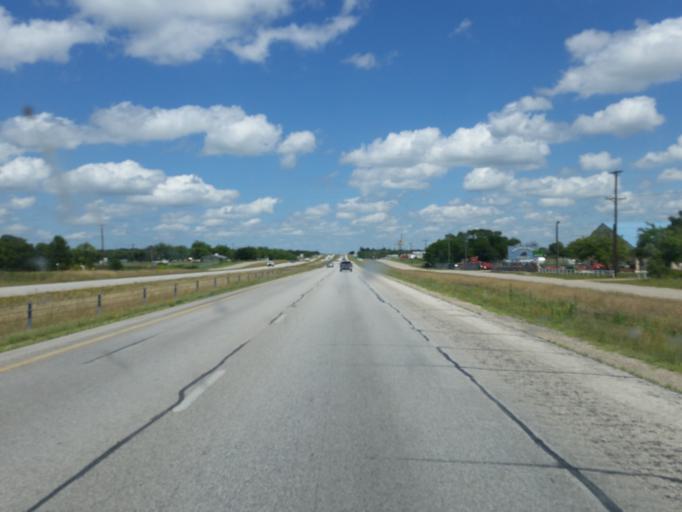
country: US
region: Texas
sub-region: Callahan County
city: Clyde
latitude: 32.4105
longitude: -99.4794
